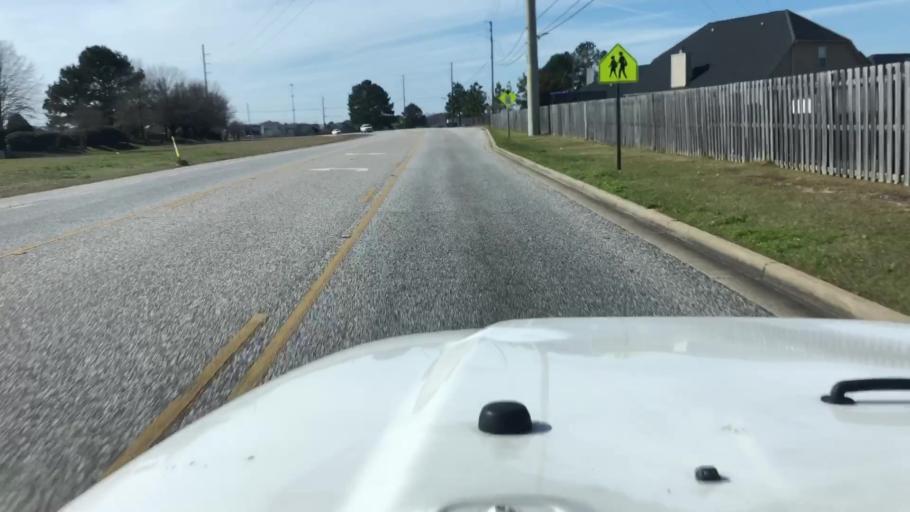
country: US
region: Alabama
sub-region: Elmore County
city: Blue Ridge
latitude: 32.3909
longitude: -86.1765
